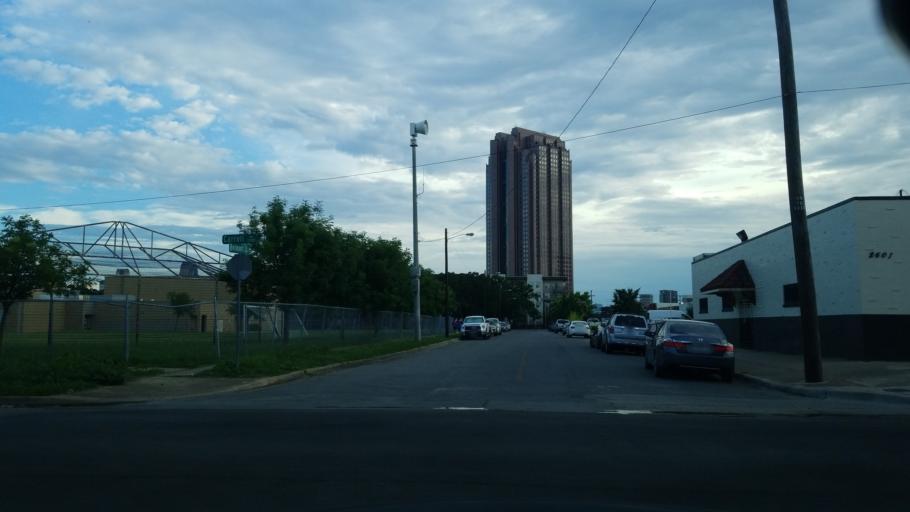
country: US
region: Texas
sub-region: Dallas County
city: Highland Park
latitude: 32.8093
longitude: -96.7878
